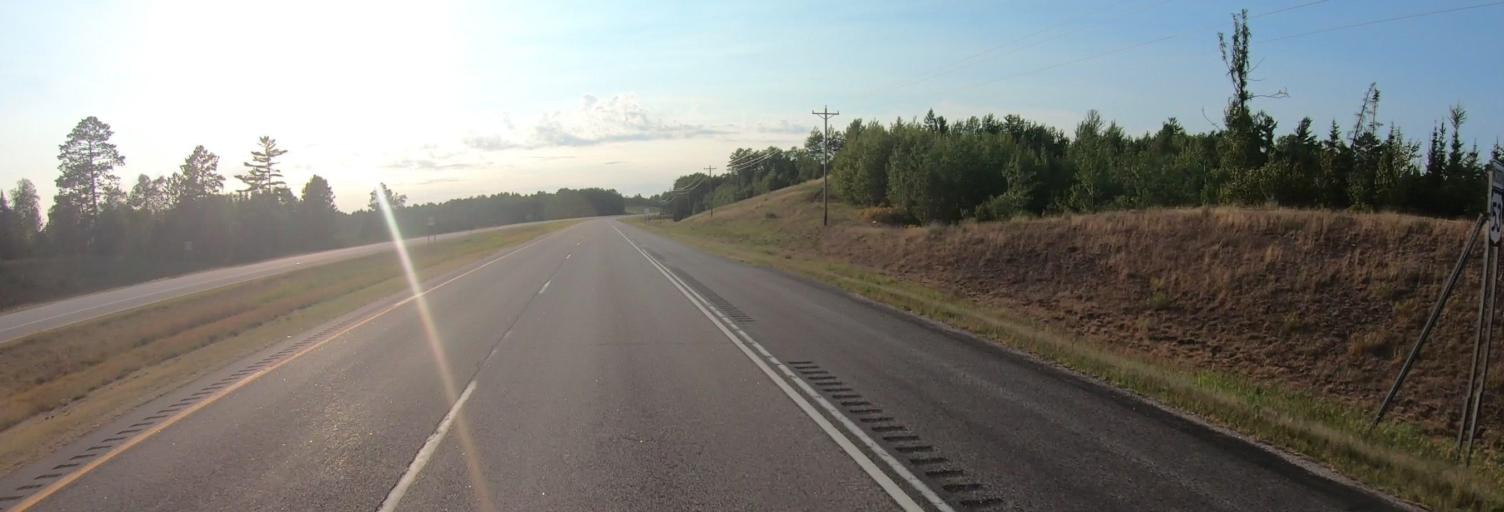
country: US
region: Minnesota
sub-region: Saint Louis County
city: Mountain Iron
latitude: 47.6673
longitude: -92.6294
